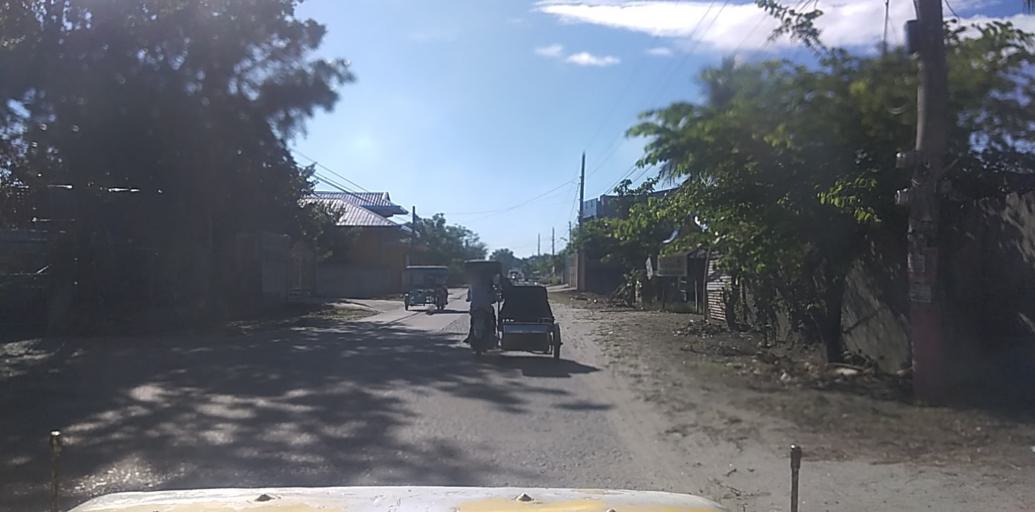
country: PH
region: Central Luzon
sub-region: Province of Pampanga
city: Mexico
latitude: 15.0801
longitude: 120.7172
